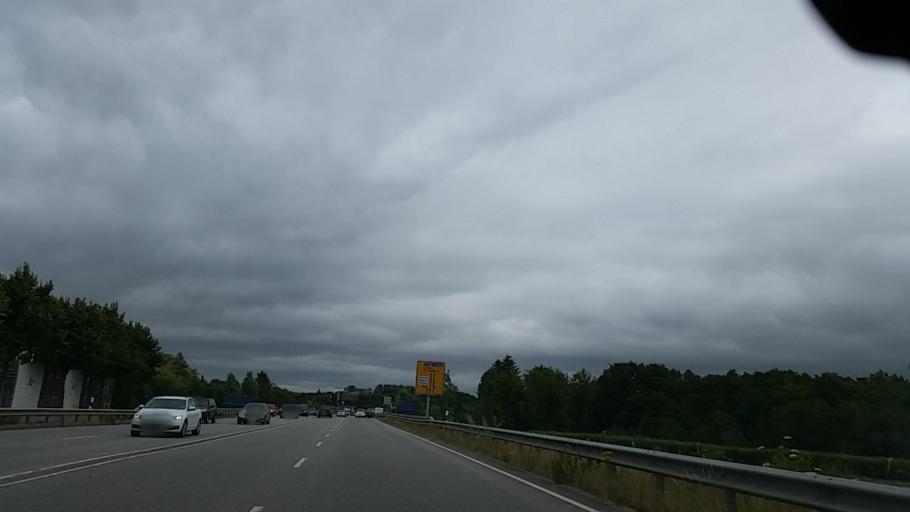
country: DE
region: Schleswig-Holstein
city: Windeby
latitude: 54.4710
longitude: 9.8271
